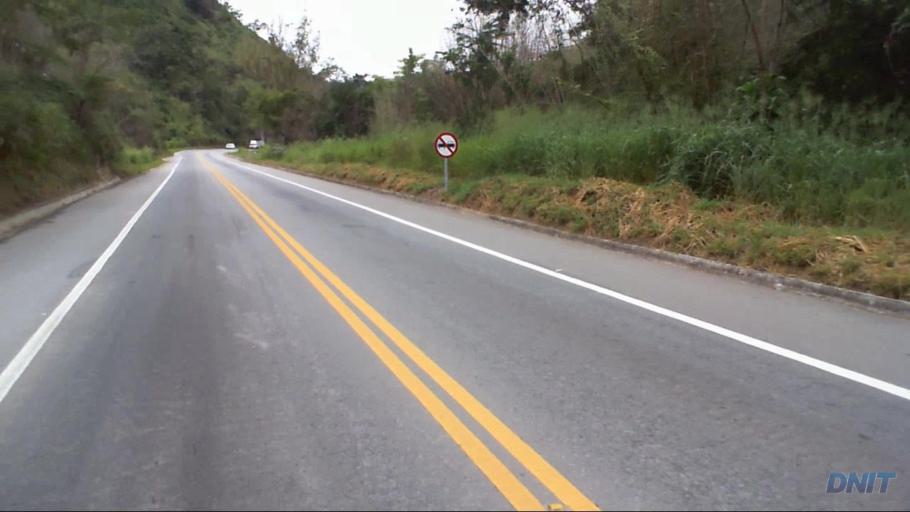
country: BR
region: Minas Gerais
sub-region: Timoteo
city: Timoteo
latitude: -19.6371
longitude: -42.8242
